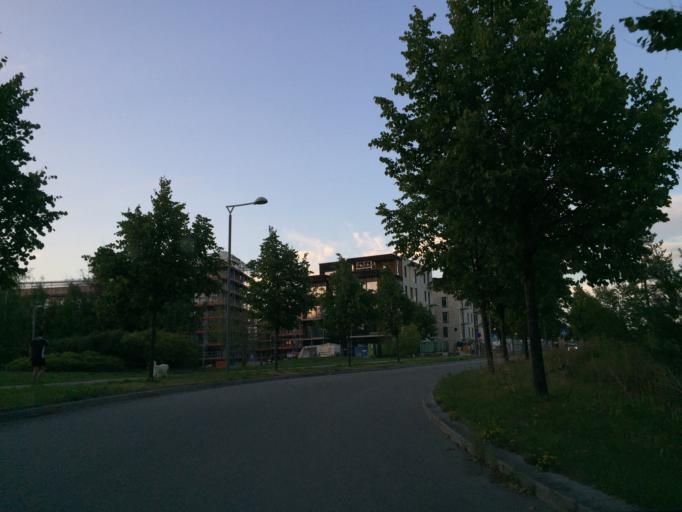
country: NO
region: Akershus
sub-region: Baerum
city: Lysaker
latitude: 59.8975
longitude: 10.6086
